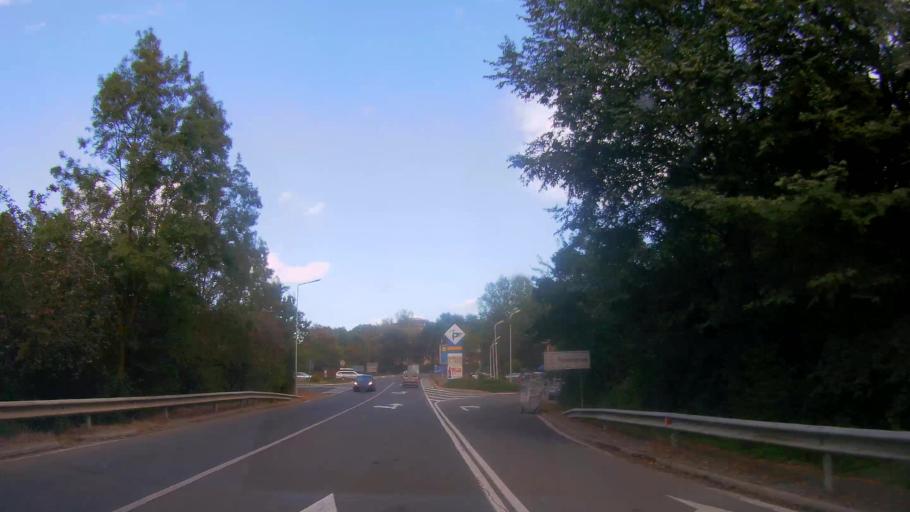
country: BG
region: Burgas
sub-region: Obshtina Primorsko
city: Primorsko
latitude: 42.2648
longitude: 27.7437
